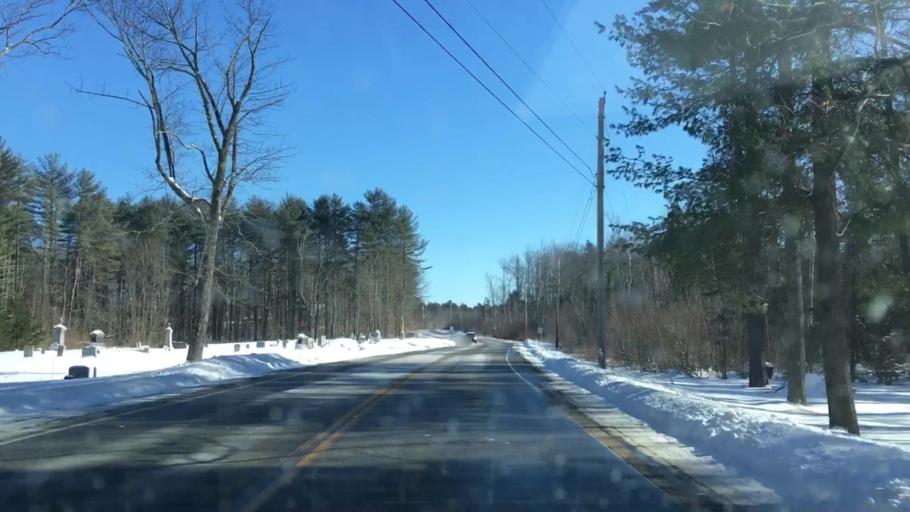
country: US
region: Maine
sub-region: Androscoggin County
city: Lisbon Falls
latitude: 44.0256
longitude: -70.0723
